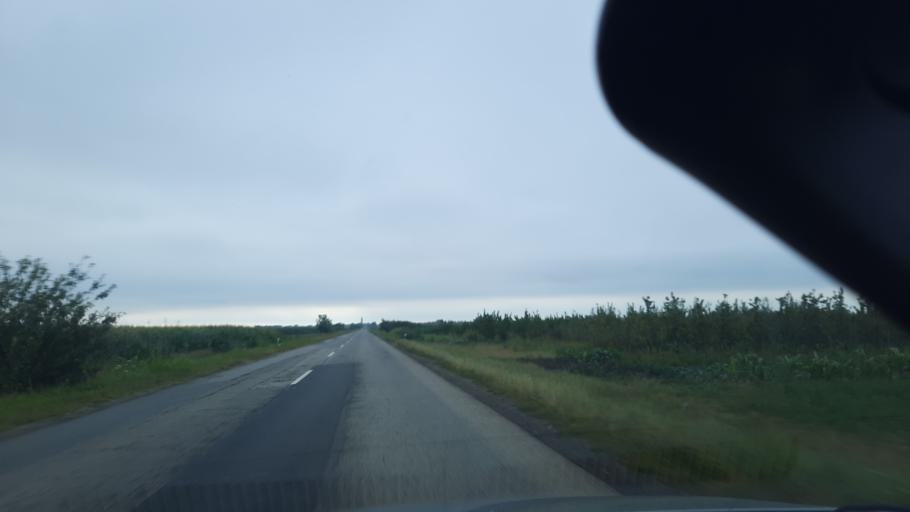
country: RS
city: Farkazdin
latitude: 45.1960
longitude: 20.4512
